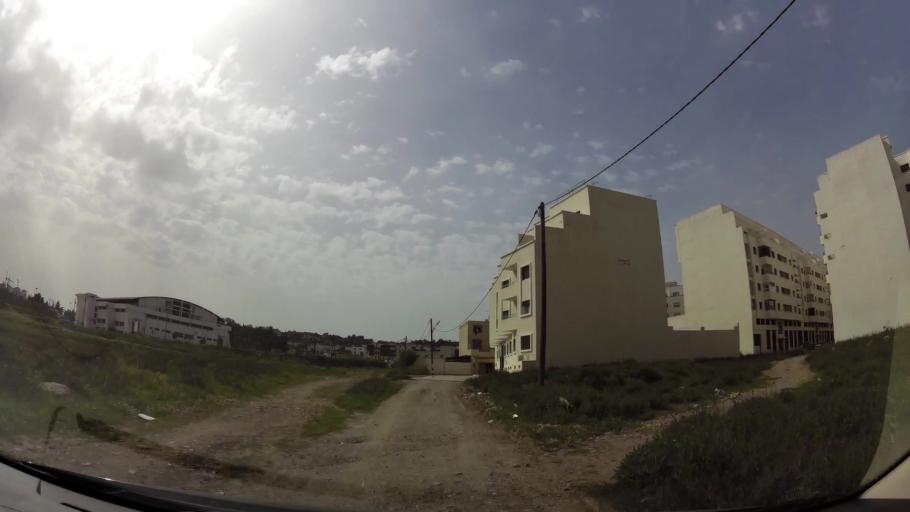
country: MA
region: Tanger-Tetouan
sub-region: Tanger-Assilah
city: Boukhalef
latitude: 35.7459
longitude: -5.8583
